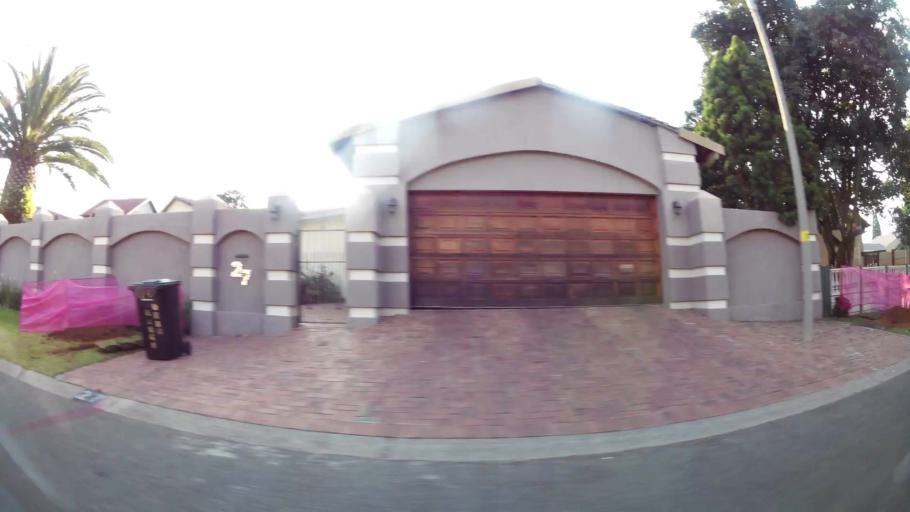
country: ZA
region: Gauteng
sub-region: City of Johannesburg Metropolitan Municipality
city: Modderfontein
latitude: -26.0791
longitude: 28.2205
